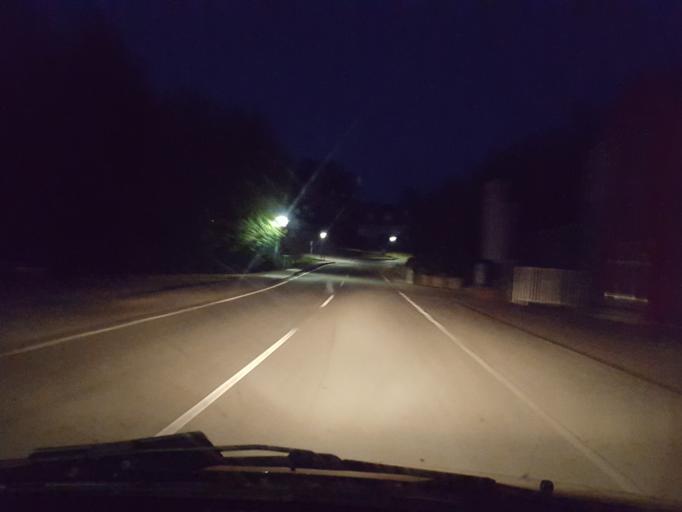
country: AT
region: Lower Austria
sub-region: Politischer Bezirk Scheibbs
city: Sankt Georgen an der Leys
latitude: 48.0298
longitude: 15.2167
